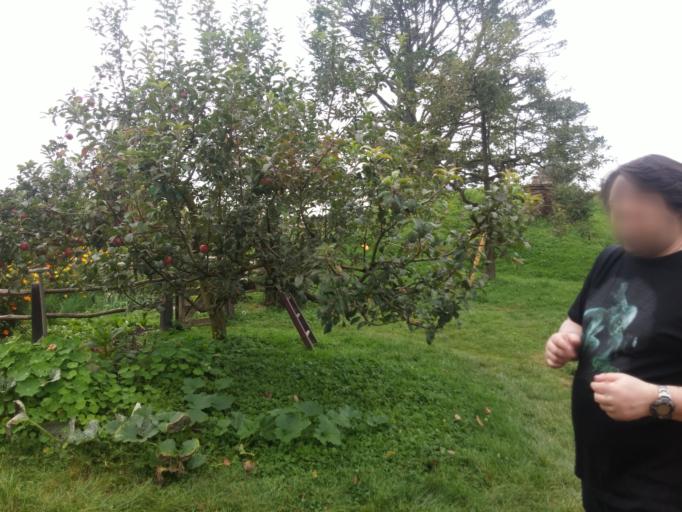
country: NZ
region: Waikato
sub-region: Matamata-Piako District
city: Matamata
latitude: -37.8575
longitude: 175.6810
